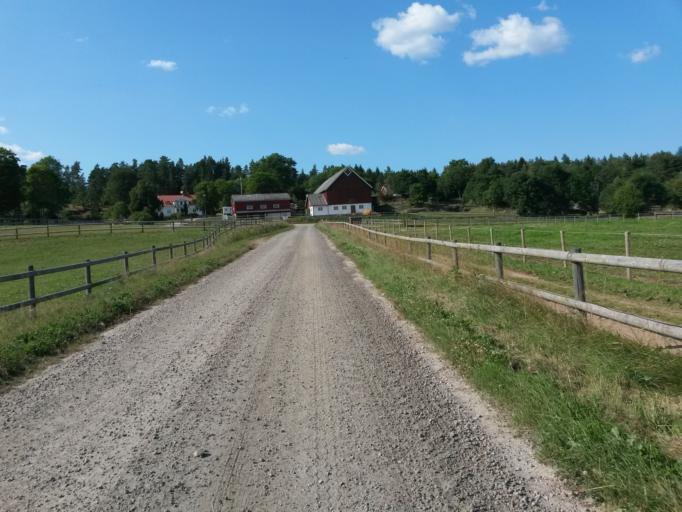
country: SE
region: Vaestra Goetaland
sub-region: Vargarda Kommun
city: Jonstorp
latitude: 57.9951
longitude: 12.6506
